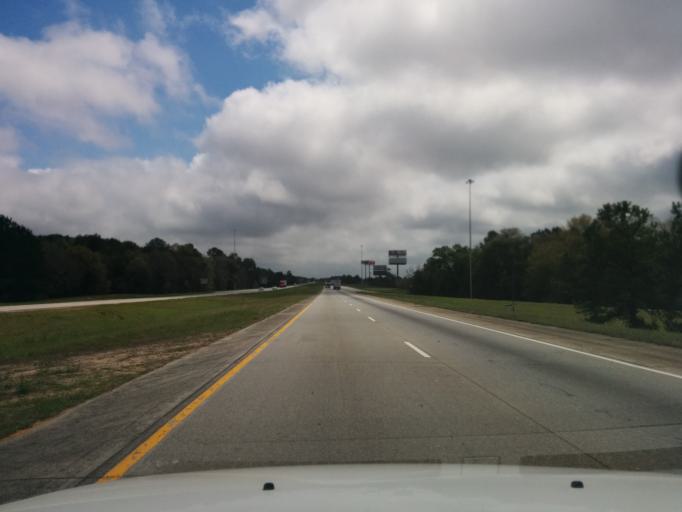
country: US
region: Georgia
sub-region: Toombs County
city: Lyons
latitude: 32.3999
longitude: -82.3058
